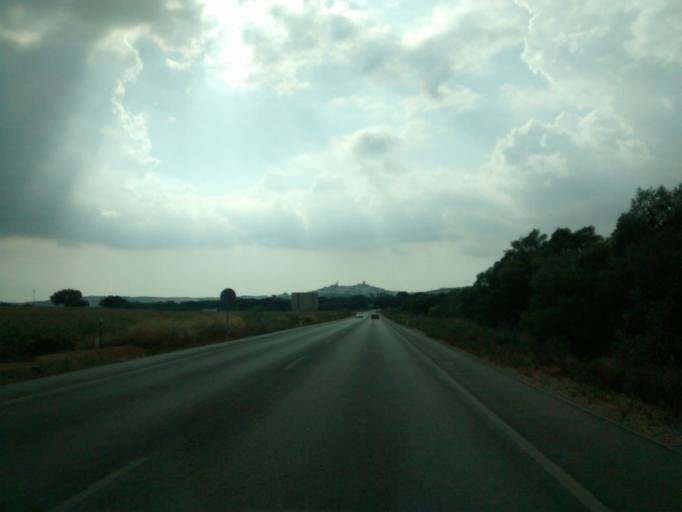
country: ES
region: Andalusia
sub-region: Provincia de Cadiz
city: Arcos de la Frontera
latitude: 36.7500
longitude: -5.7661
